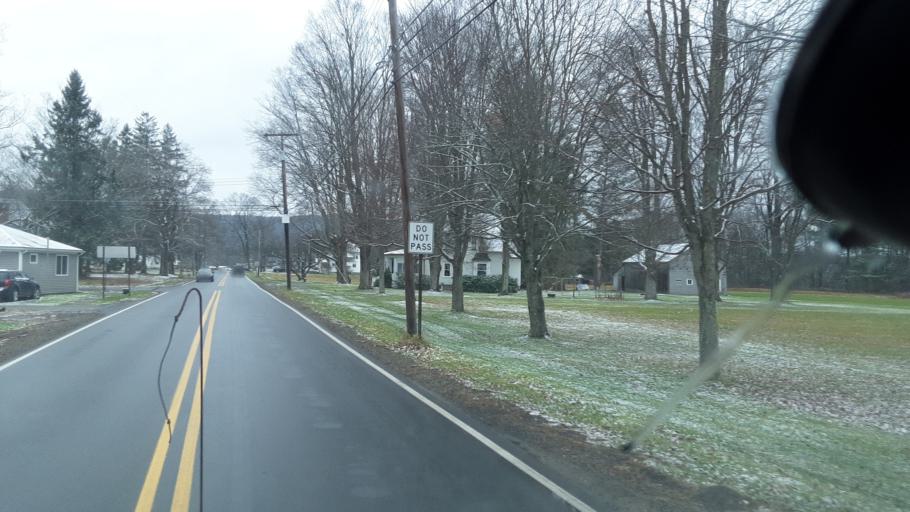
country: US
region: Pennsylvania
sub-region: Potter County
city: Shinglehouse
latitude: 41.9667
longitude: -78.1871
